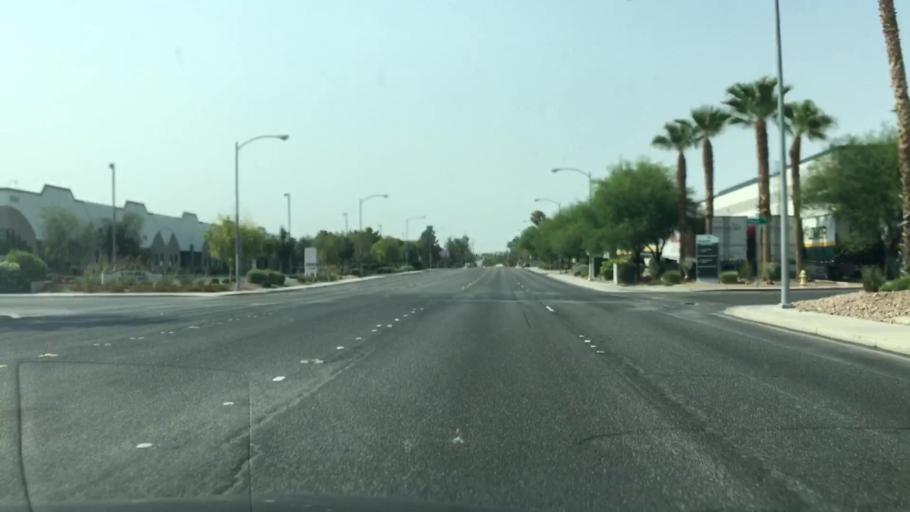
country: US
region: Nevada
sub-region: Clark County
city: Whitney
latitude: 36.0752
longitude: -115.0917
